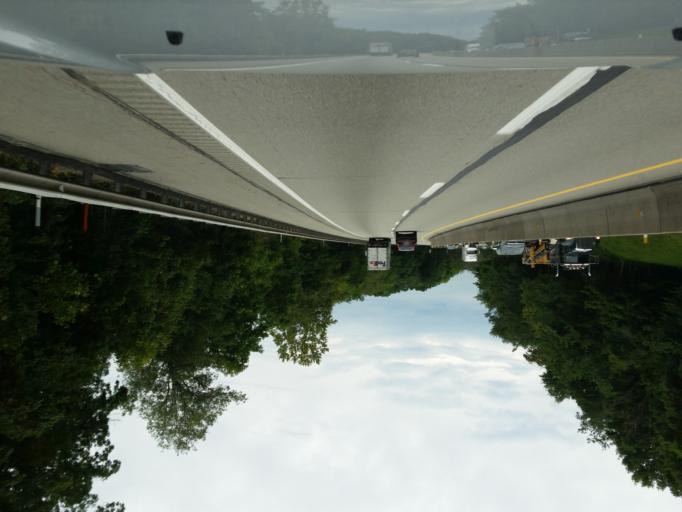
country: US
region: Pennsylvania
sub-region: Westmoreland County
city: Irwin
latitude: 40.3445
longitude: -79.6906
